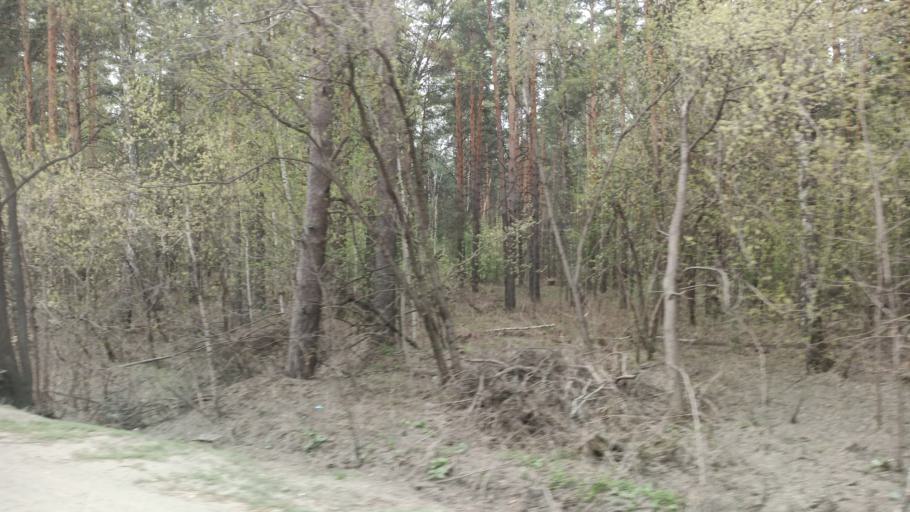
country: RU
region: Altai Krai
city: Yuzhnyy
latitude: 53.2800
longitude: 83.7172
